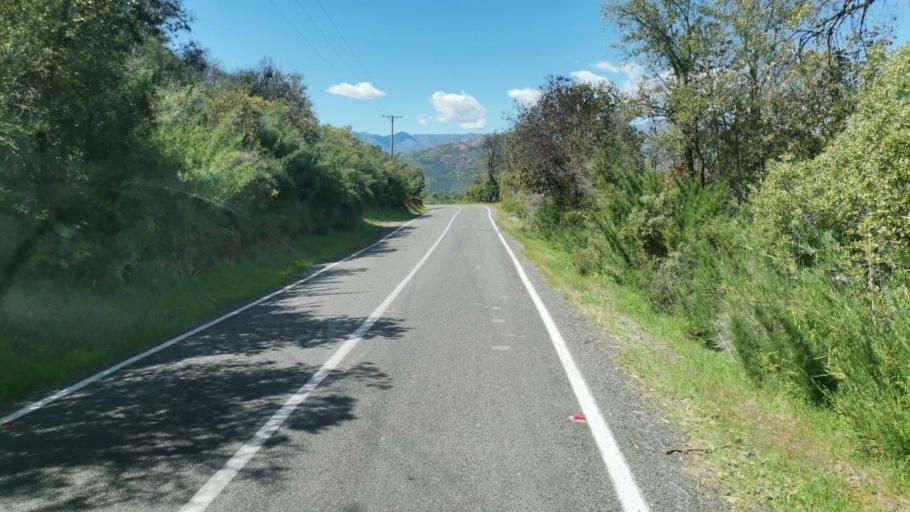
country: CL
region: Valparaiso
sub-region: Provincia de Marga Marga
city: Limache
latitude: -33.1939
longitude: -71.2070
